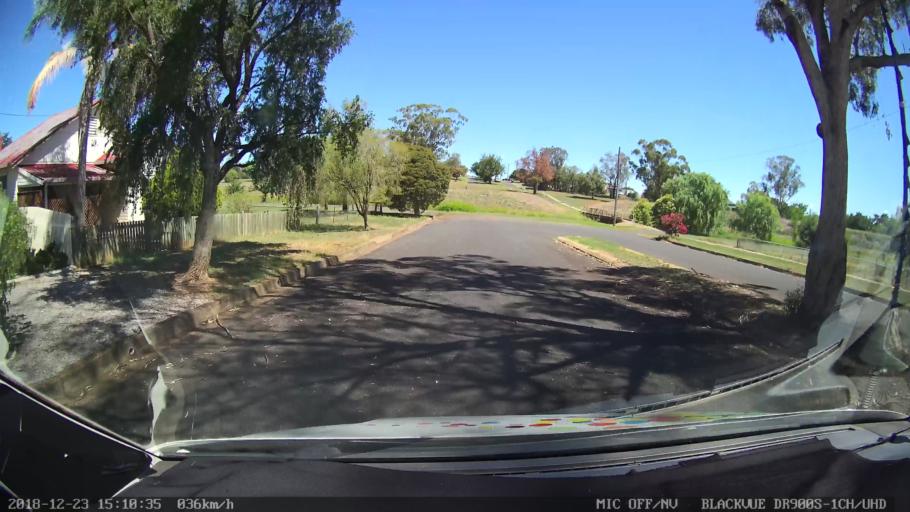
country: AU
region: New South Wales
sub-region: Tamworth Municipality
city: Manilla
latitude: -30.7511
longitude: 150.7218
